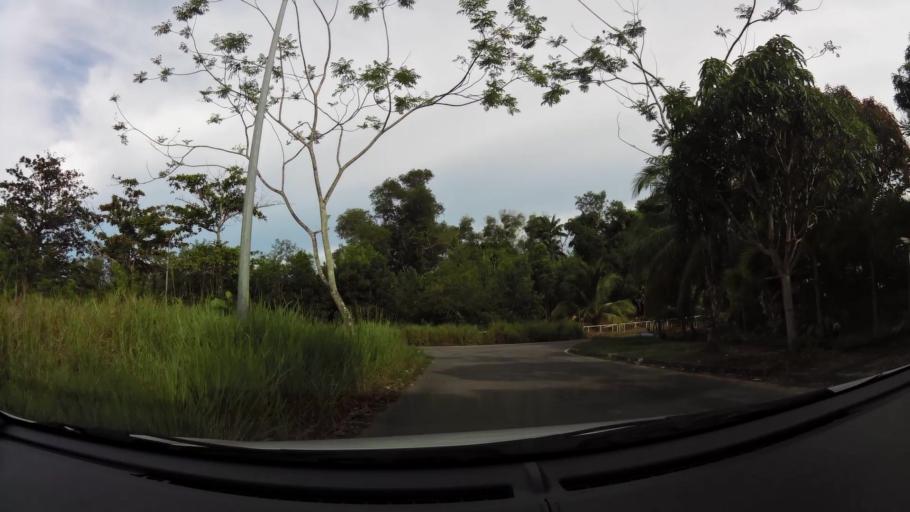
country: BN
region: Brunei and Muara
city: Bandar Seri Begawan
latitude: 4.9721
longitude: 115.0306
